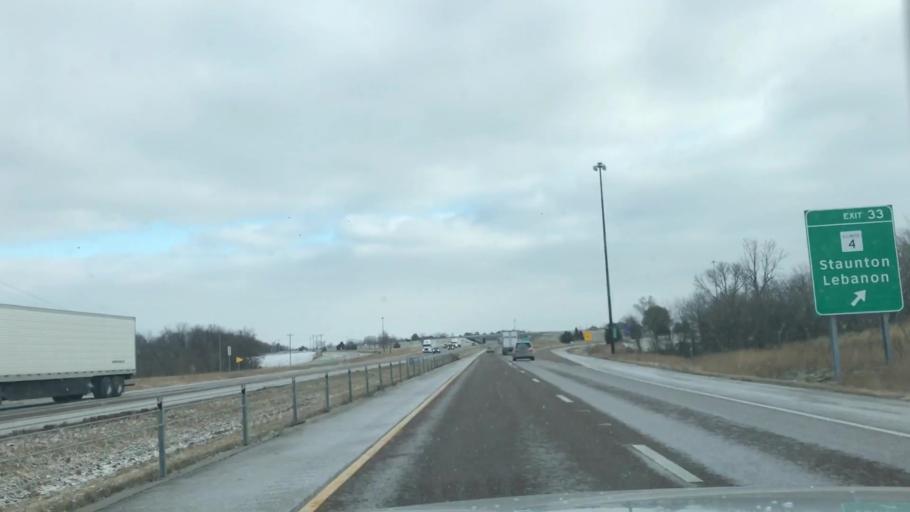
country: US
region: Illinois
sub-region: Madison County
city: Worden
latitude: 38.9274
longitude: -89.8056
